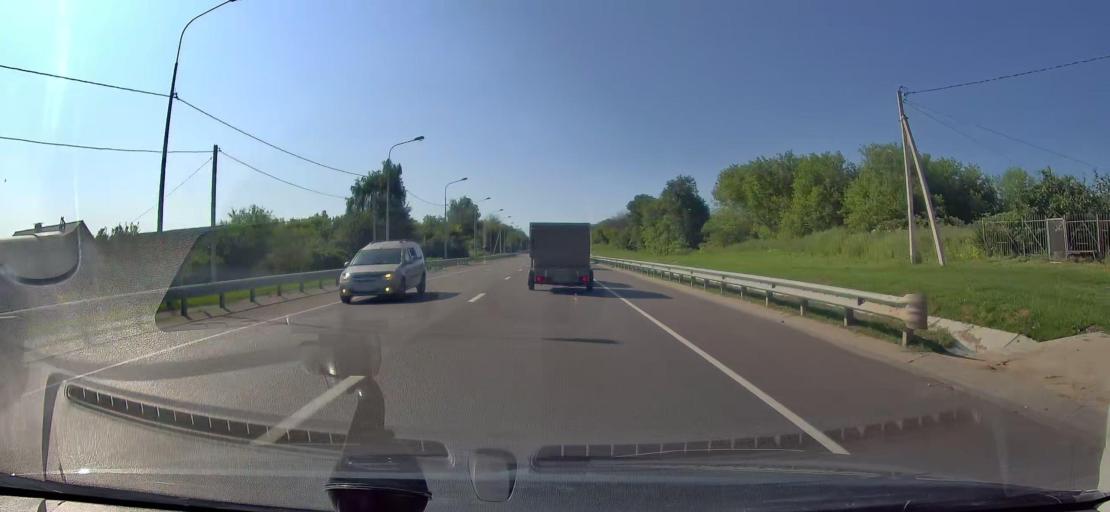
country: RU
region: Orjol
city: Kromy
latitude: 52.6196
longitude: 35.7598
